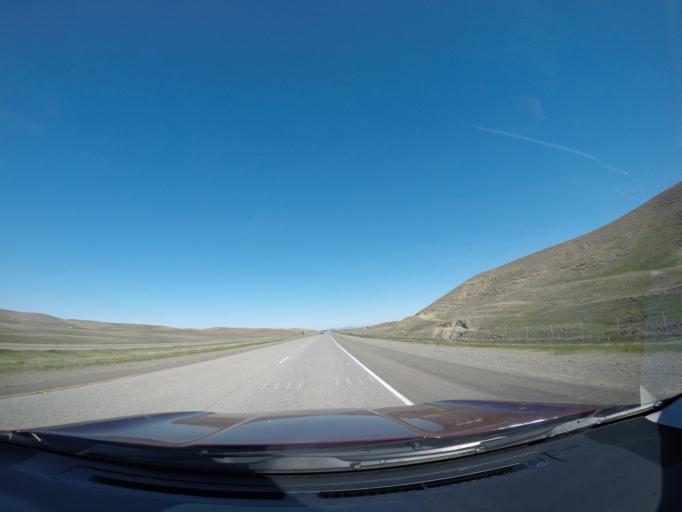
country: US
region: California
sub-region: Yolo County
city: Dunnigan
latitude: 38.7911
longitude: -121.9435
